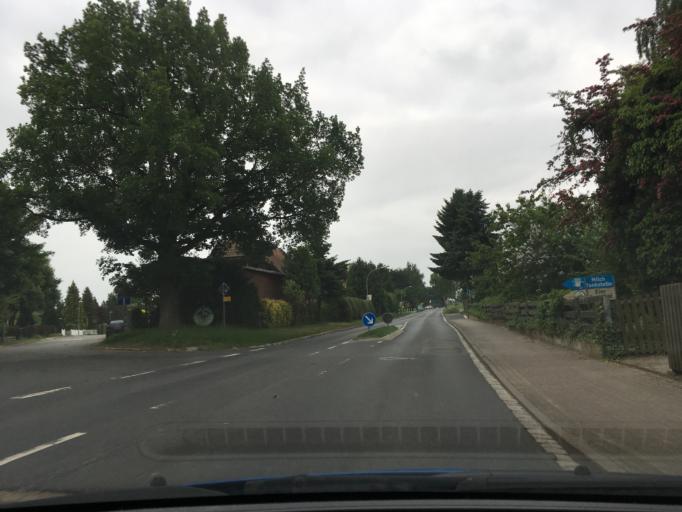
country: DE
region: Lower Saxony
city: Wulfsen
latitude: 53.3434
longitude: 10.1483
